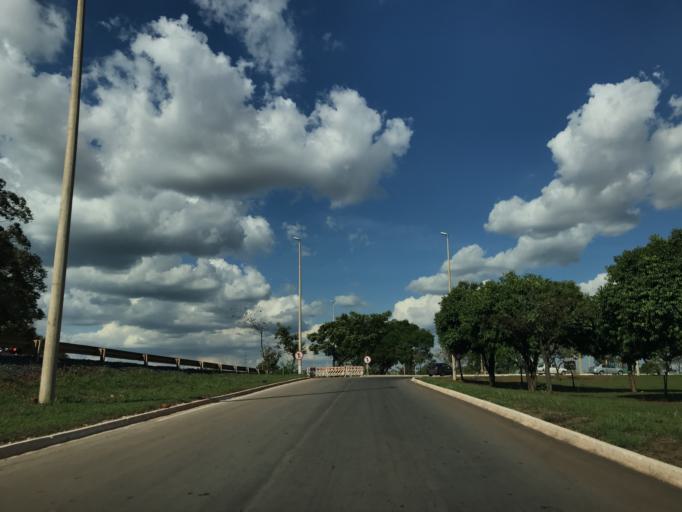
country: BR
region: Federal District
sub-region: Brasilia
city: Brasilia
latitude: -15.7918
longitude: -48.0543
